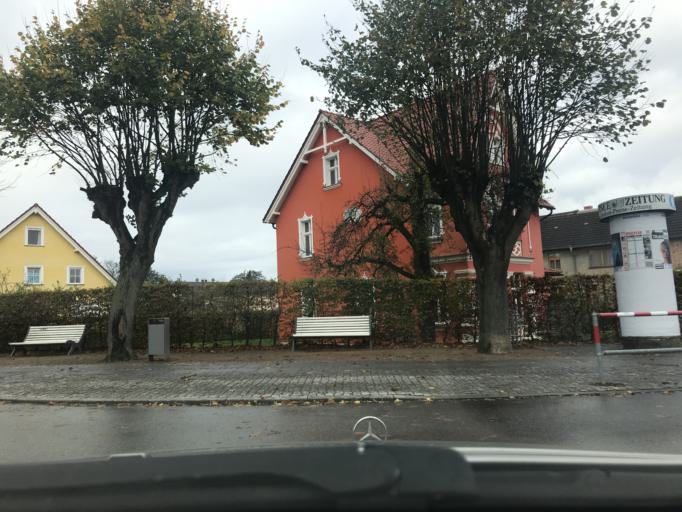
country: DE
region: Mecklenburg-Vorpommern
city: Ostseebad Zinnowitz
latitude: 54.0749
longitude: 13.9063
